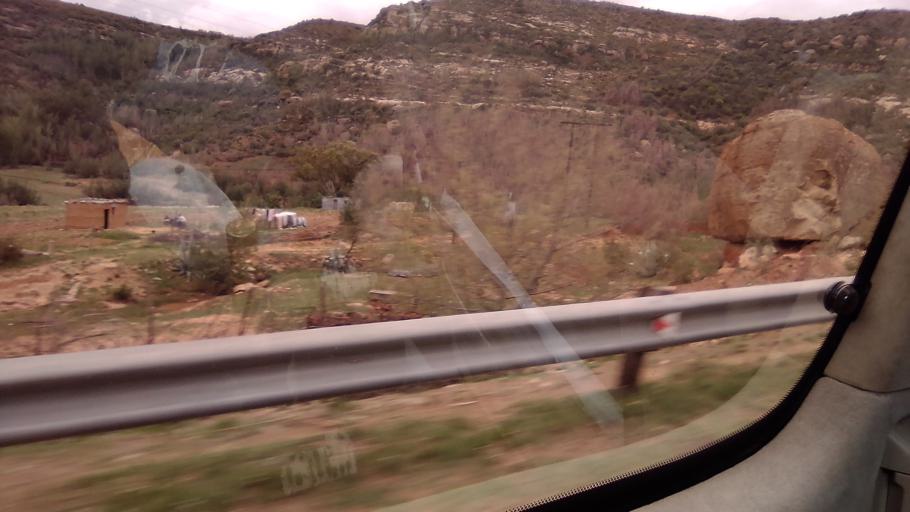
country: LS
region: Berea
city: Teyateyaneng
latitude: -29.3316
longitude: 27.6992
